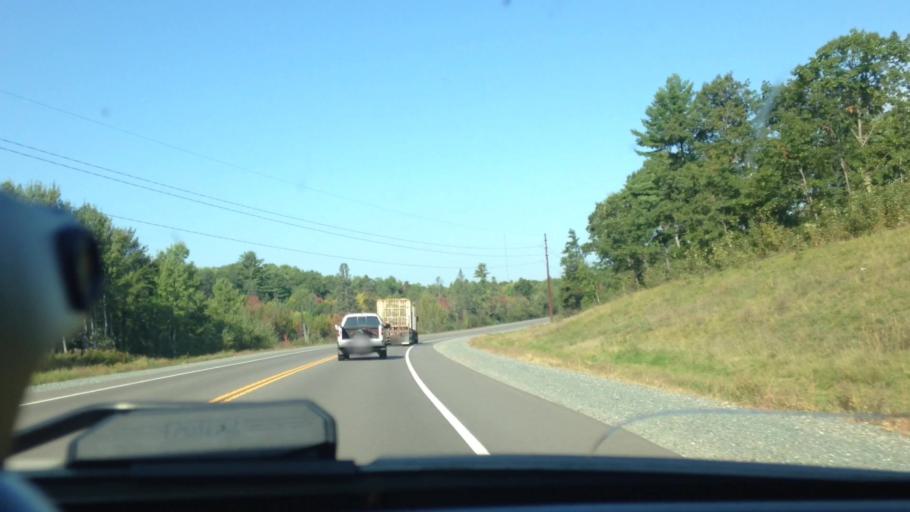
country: US
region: Michigan
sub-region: Dickinson County
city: Iron Mountain
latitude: 45.8761
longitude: -88.1144
